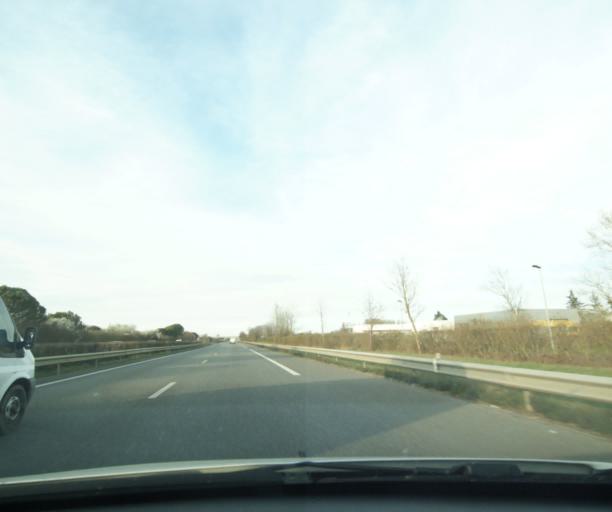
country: FR
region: Midi-Pyrenees
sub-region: Departement de la Haute-Garonne
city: Le Fauga
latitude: 43.3938
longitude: 1.2871
